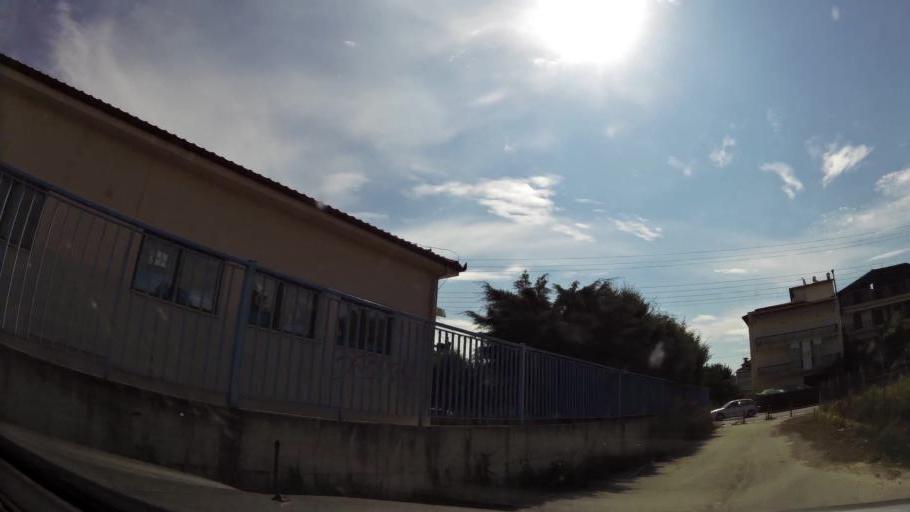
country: GR
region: Central Macedonia
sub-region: Nomos Pierias
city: Katerini
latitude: 40.2752
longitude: 22.4916
